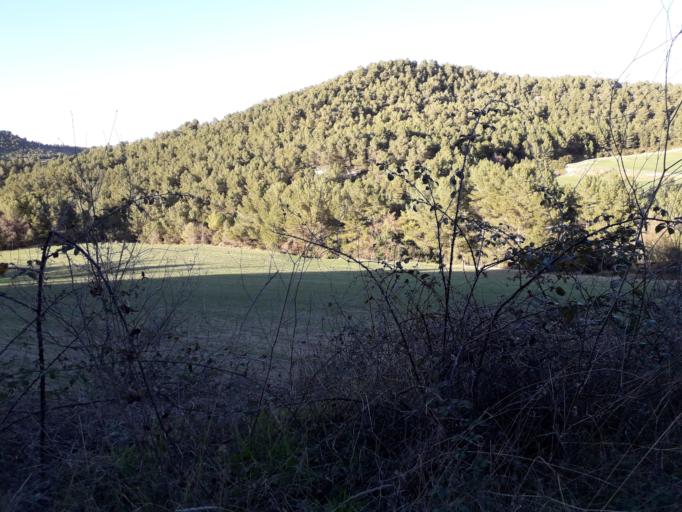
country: ES
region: Catalonia
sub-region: Provincia de Barcelona
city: Bellprat
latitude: 41.5419
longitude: 1.4604
